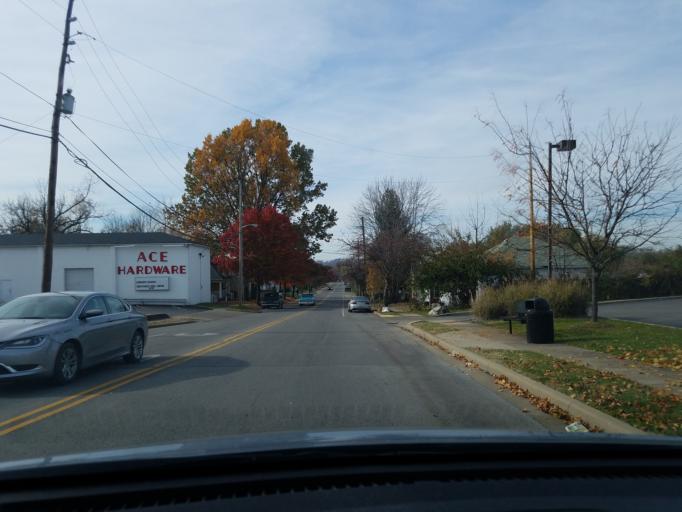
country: US
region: Indiana
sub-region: Floyd County
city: New Albany
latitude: 38.3043
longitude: -85.8131
